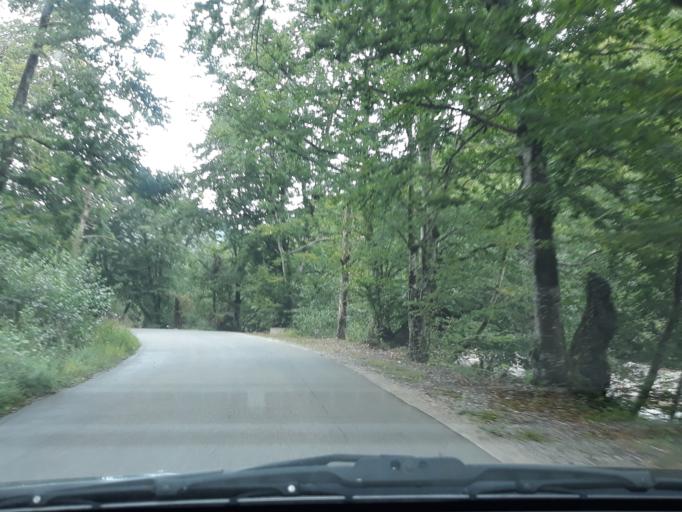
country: RO
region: Bihor
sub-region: Comuna Pietroasa
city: Pietroasa
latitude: 46.5885
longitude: 22.5954
